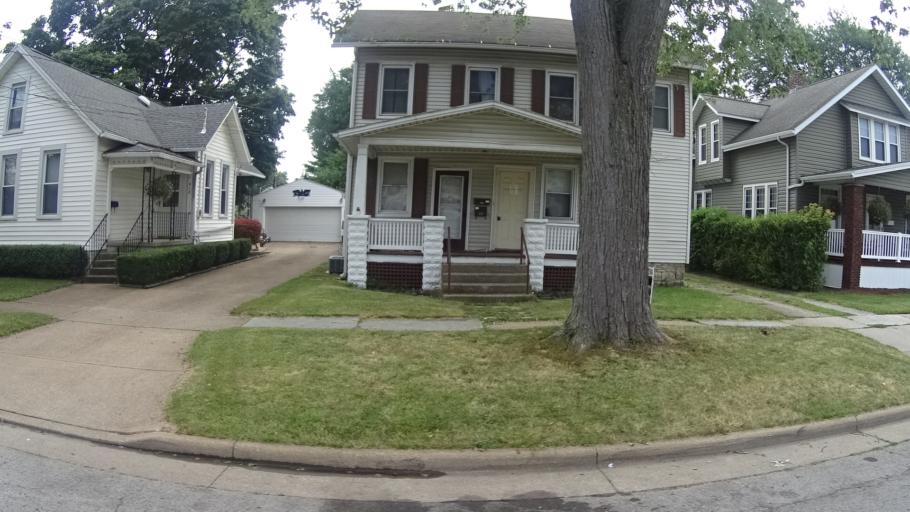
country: US
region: Ohio
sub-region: Erie County
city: Sandusky
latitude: 41.4472
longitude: -82.7247
